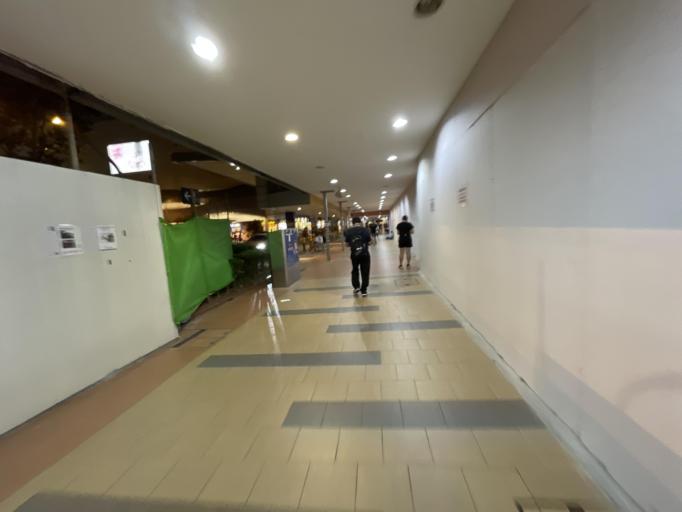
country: MY
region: Johor
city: Kampung Pasir Gudang Baru
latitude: 1.3731
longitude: 103.9495
